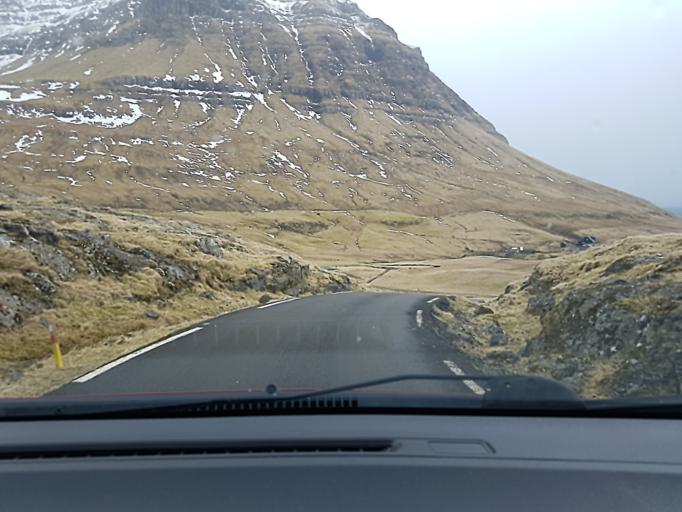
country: FO
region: Streymoy
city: Kollafjordhur
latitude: 62.0429
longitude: -6.9261
